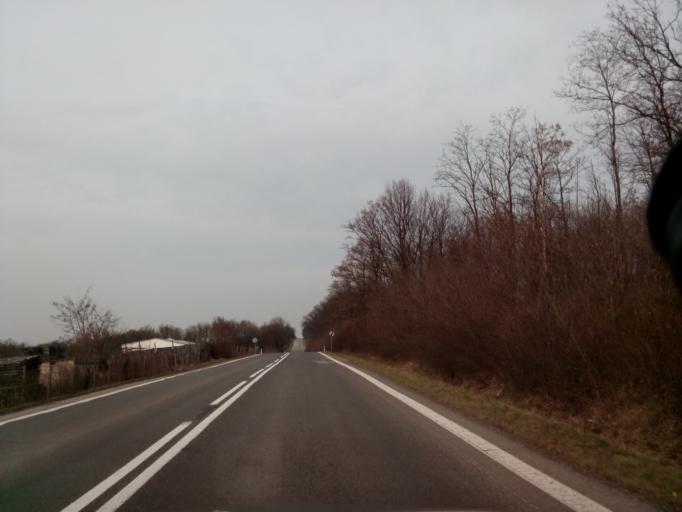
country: HU
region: Borsod-Abauj-Zemplen
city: Satoraljaujhely
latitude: 48.5014
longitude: 21.6528
